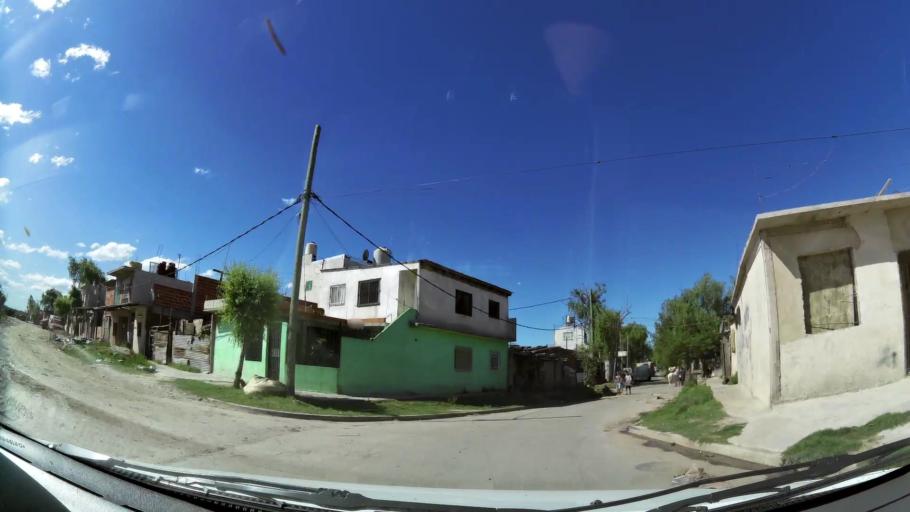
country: AR
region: Buenos Aires
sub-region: Partido de Tigre
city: Tigre
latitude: -34.5091
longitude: -58.5881
